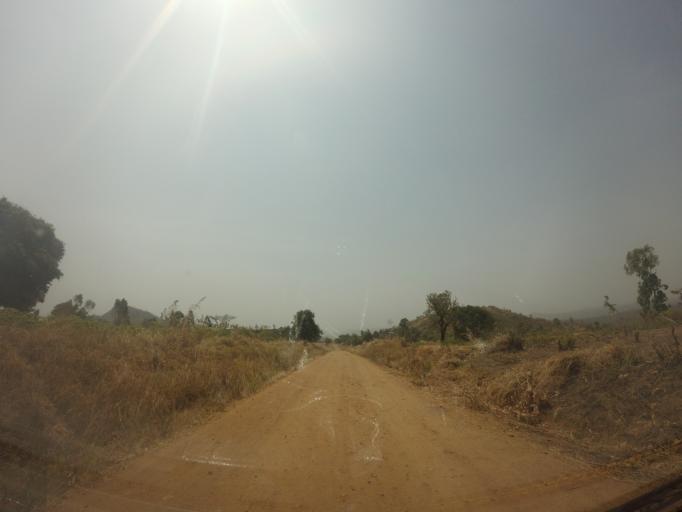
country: UG
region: Northern Region
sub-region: Arua District
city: Arua
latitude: 2.9313
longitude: 30.9824
